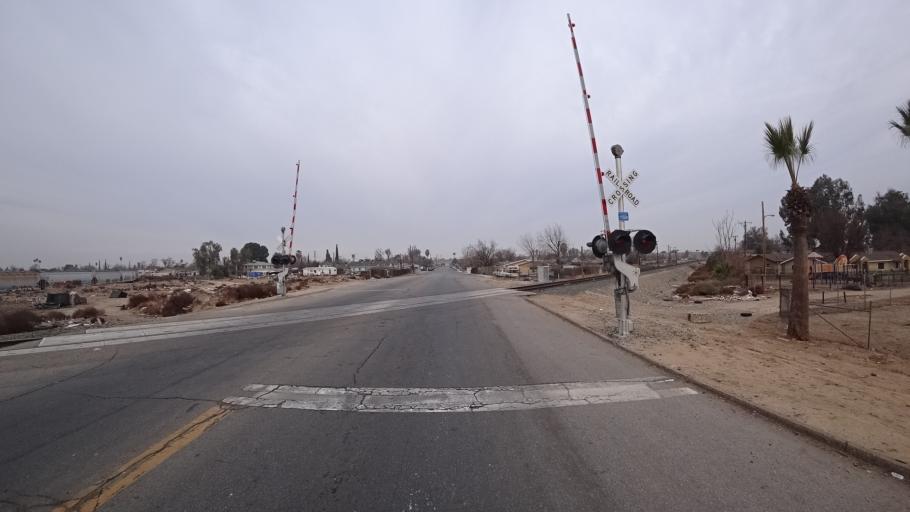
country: US
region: California
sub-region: Kern County
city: Bakersfield
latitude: 35.3473
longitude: -118.9941
